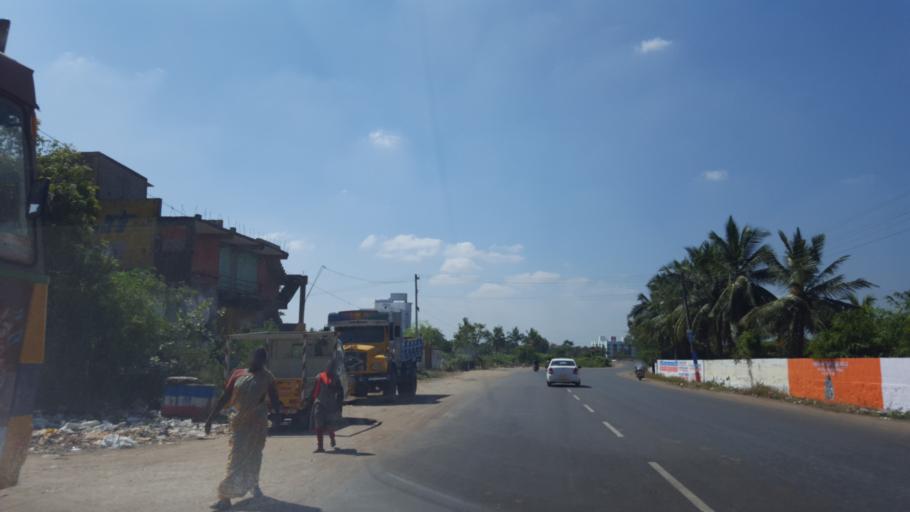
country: IN
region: Tamil Nadu
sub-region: Kancheepuram
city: Mamallapuram
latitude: 12.7137
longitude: 80.1872
